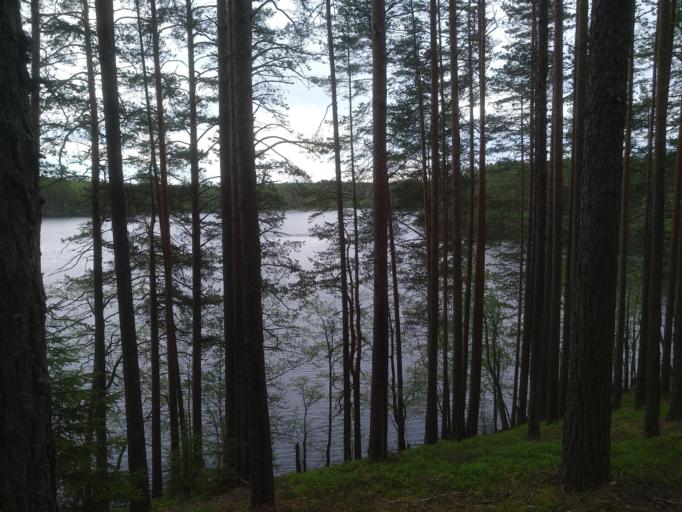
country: RU
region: Leningrad
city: Michurinskoye
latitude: 60.5949
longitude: 29.8855
